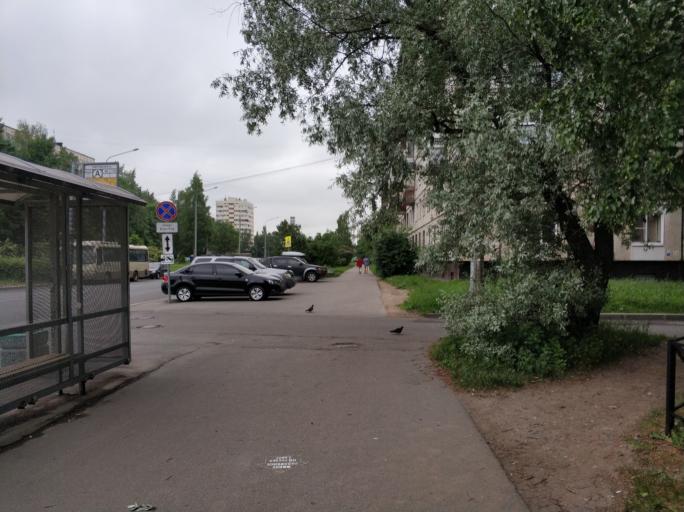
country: RU
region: St.-Petersburg
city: Grazhdanka
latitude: 60.0419
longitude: 30.4154
